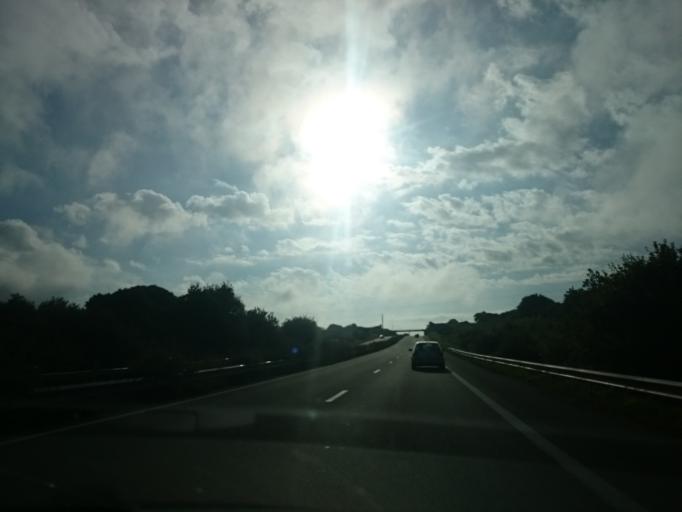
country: FR
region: Brittany
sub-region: Departement du Finistere
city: Guerlesquin
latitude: 48.5684
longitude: -3.5949
